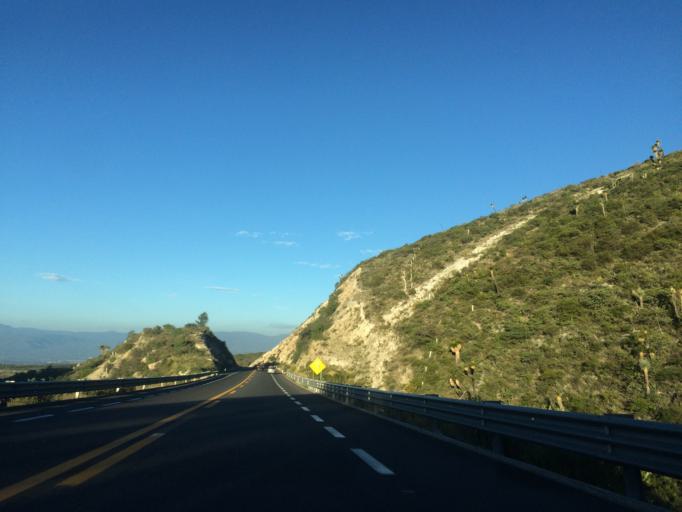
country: MX
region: Puebla
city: Chapuco
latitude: 18.6216
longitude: -97.4682
